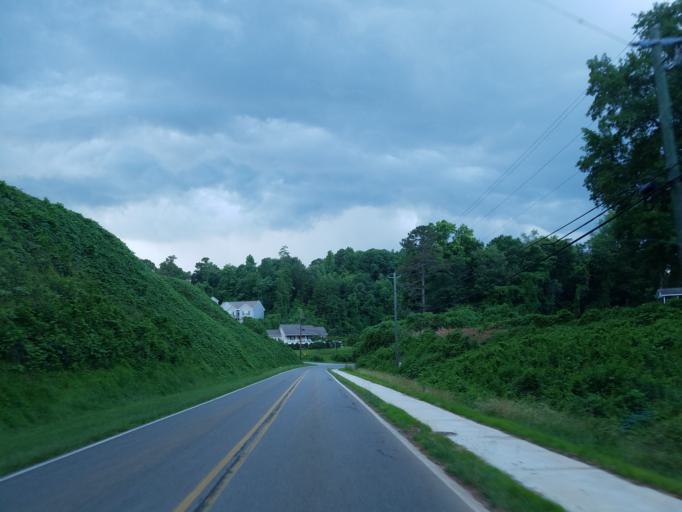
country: US
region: Georgia
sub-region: Lumpkin County
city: Dahlonega
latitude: 34.5378
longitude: -83.9836
